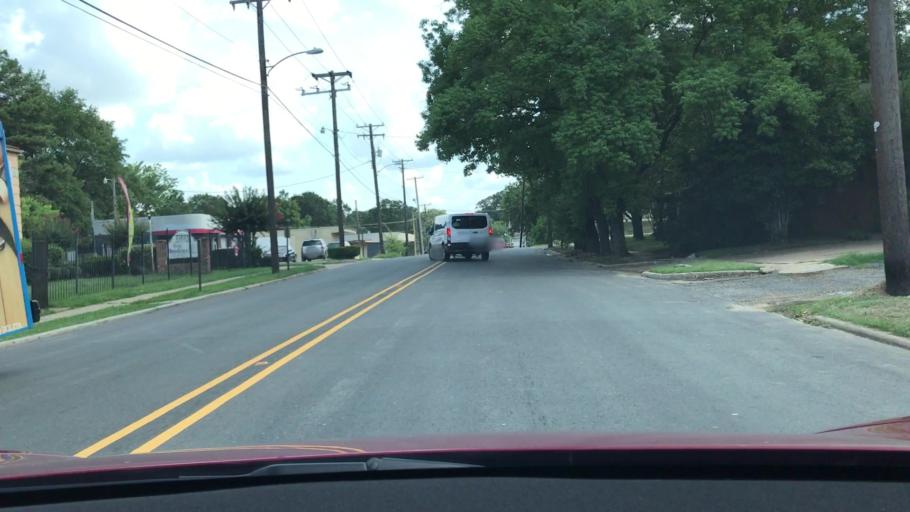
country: US
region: Louisiana
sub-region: Bossier Parish
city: Bossier City
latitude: 32.4941
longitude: -93.7333
